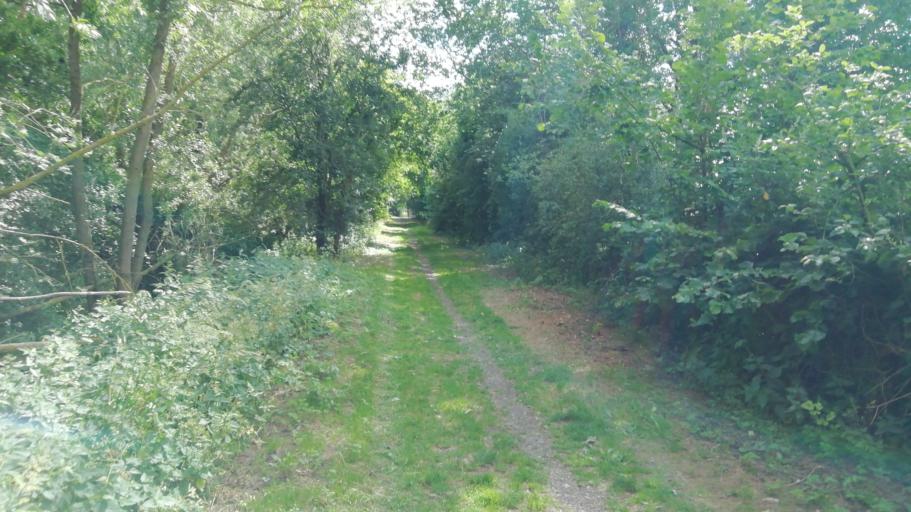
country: BE
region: Wallonia
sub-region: Province du Hainaut
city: Merbes-le-Chateau
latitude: 50.3212
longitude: 4.1680
